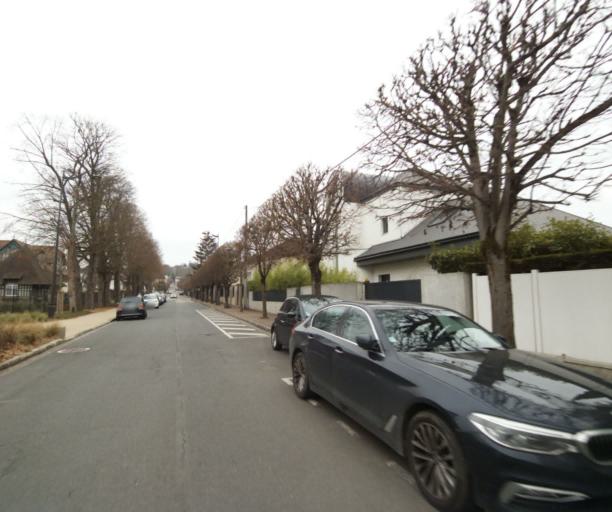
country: FR
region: Ile-de-France
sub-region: Departement des Hauts-de-Seine
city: Saint-Cloud
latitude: 48.8605
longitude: 2.1953
